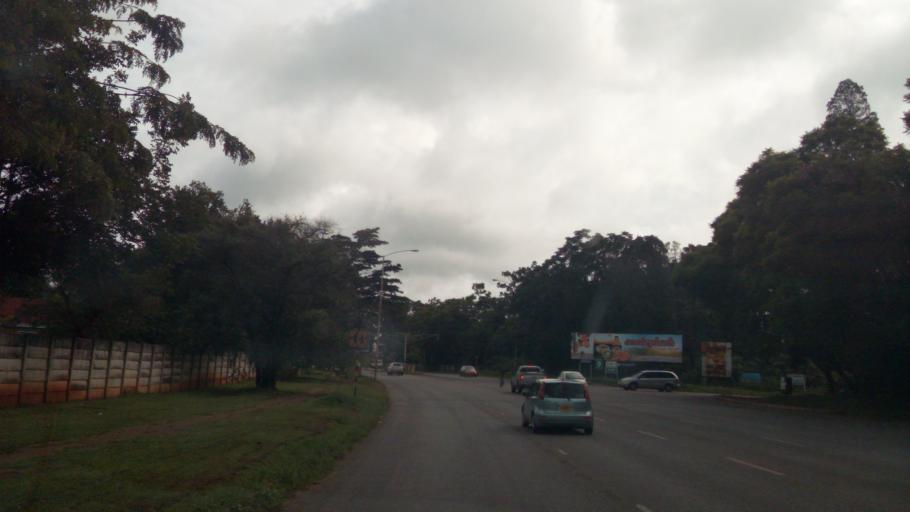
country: ZW
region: Harare
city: Harare
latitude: -17.8059
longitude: 31.0595
